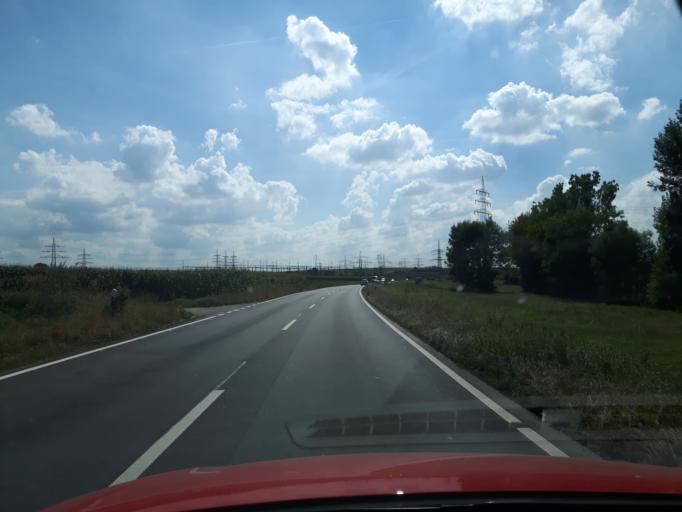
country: DE
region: Baden-Wuerttemberg
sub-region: Regierungsbezirk Stuttgart
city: Leingarten
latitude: 49.1497
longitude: 9.1556
